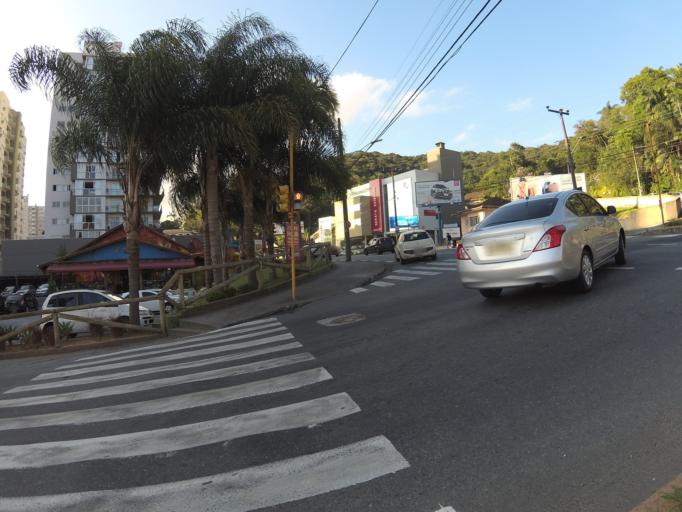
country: BR
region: Santa Catarina
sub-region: Blumenau
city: Blumenau
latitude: -26.9076
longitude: -49.0728
